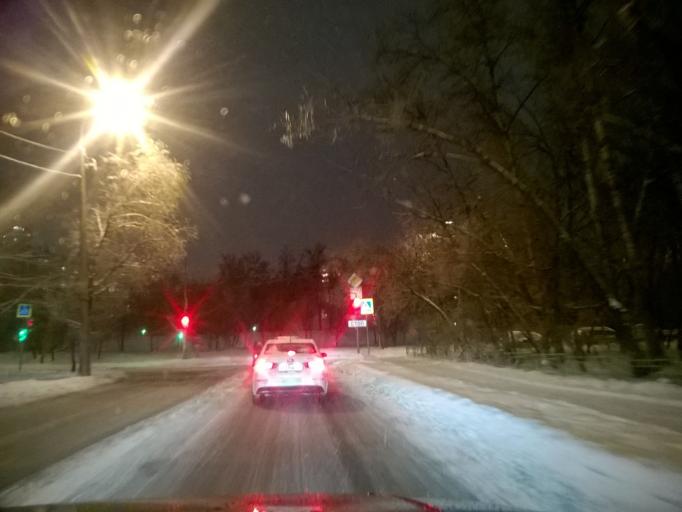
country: RU
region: Moskovskaya
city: Bol'shaya Setun'
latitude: 55.7332
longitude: 37.4359
